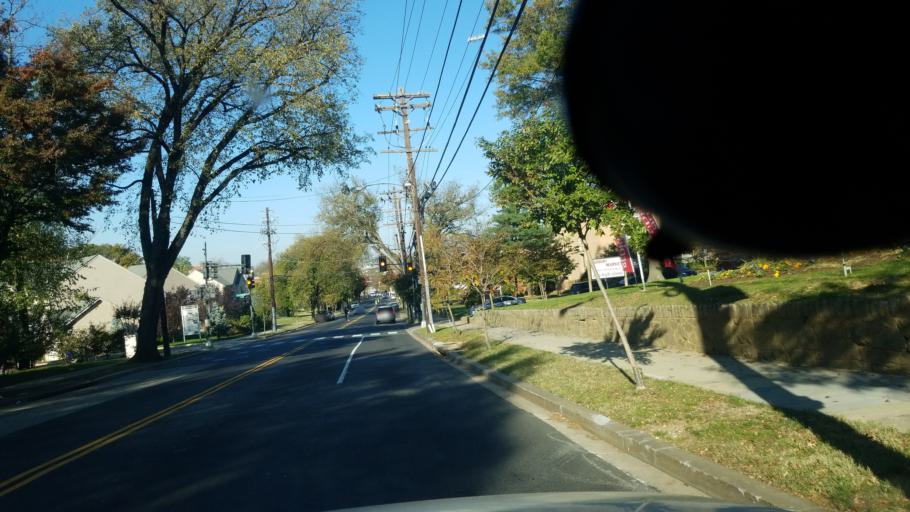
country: US
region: Maryland
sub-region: Prince George's County
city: Hillcrest Heights
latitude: 38.8638
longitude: -76.9745
